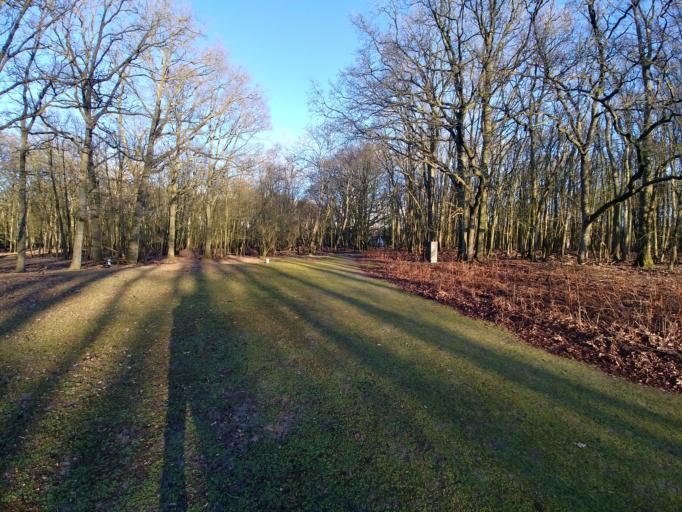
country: NL
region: North Holland
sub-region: Gemeente Bloemendaal
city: Bennebroek
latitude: 52.3445
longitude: 4.5804
